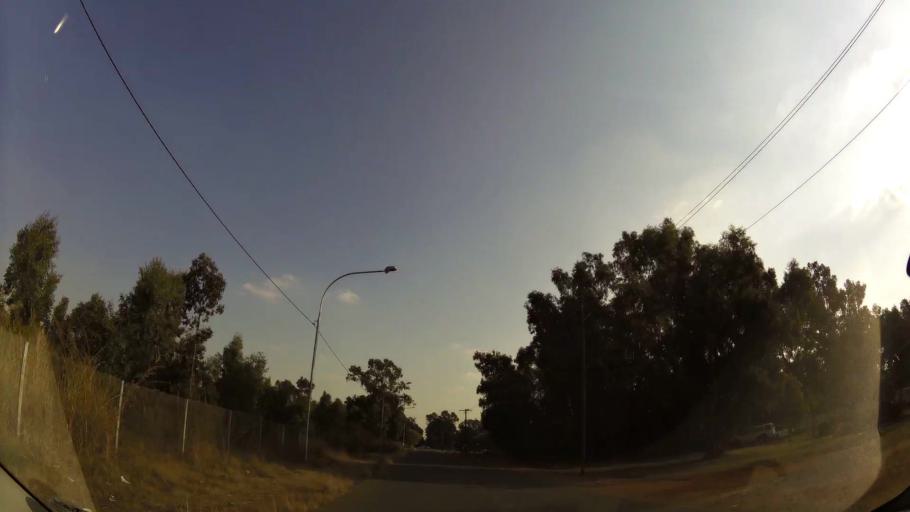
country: ZA
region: Gauteng
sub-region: Ekurhuleni Metropolitan Municipality
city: Benoni
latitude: -26.1071
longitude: 28.3743
